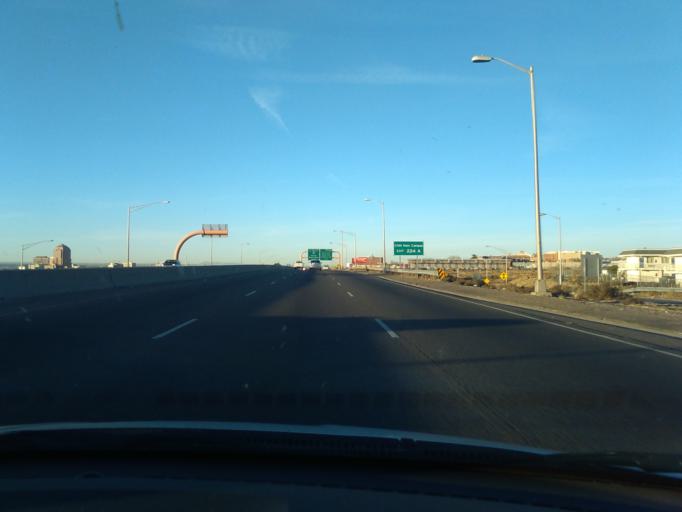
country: US
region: New Mexico
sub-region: Bernalillo County
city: Albuquerque
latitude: 35.0680
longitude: -106.6393
